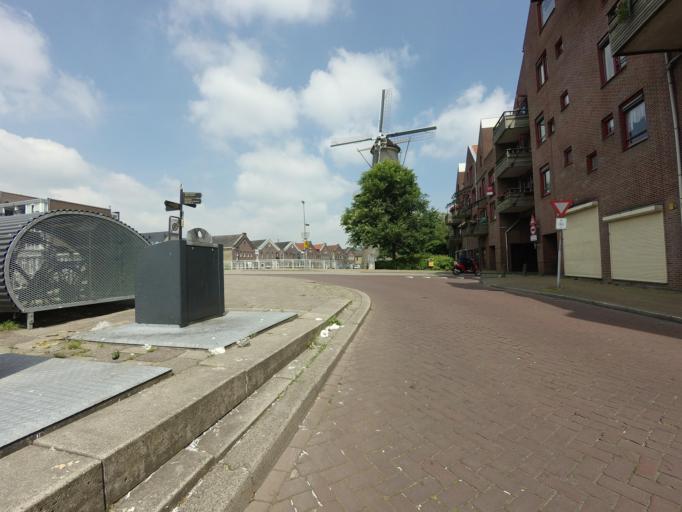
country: NL
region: South Holland
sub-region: Gemeente Schiedam
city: Schiedam
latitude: 51.9201
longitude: 4.3962
